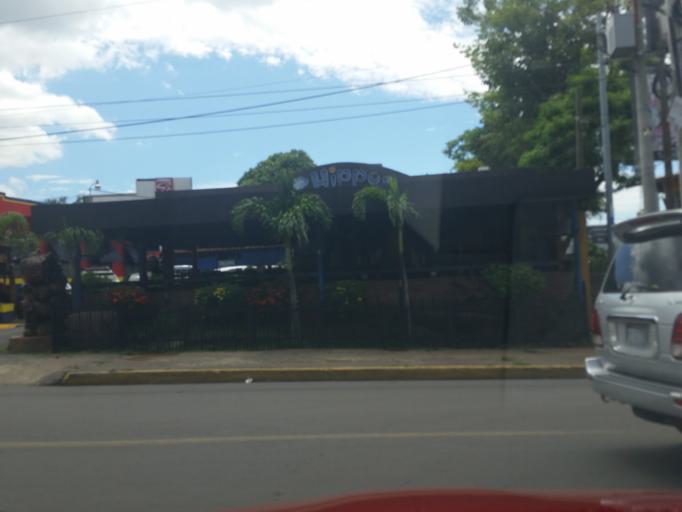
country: NI
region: Managua
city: Managua
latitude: 12.1227
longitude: -86.2658
